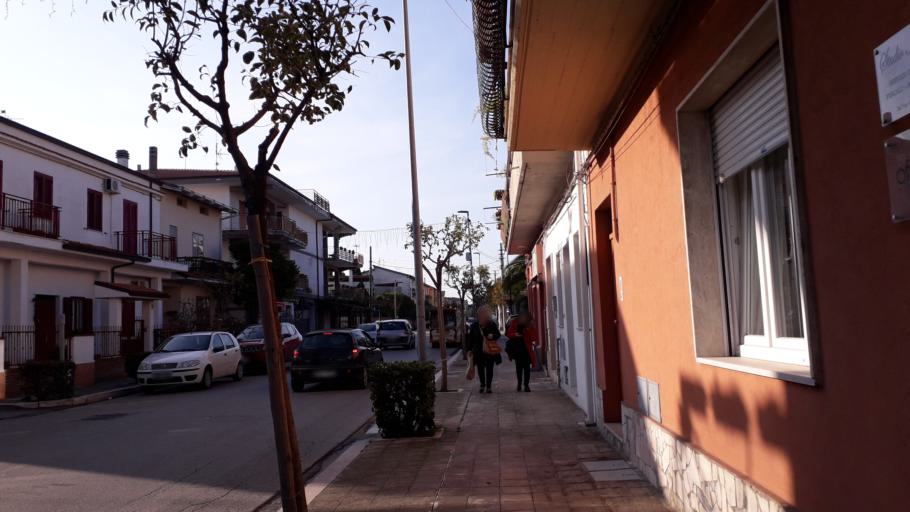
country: IT
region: Molise
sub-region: Provincia di Campobasso
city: Campomarino
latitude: 41.9562
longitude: 15.0325
